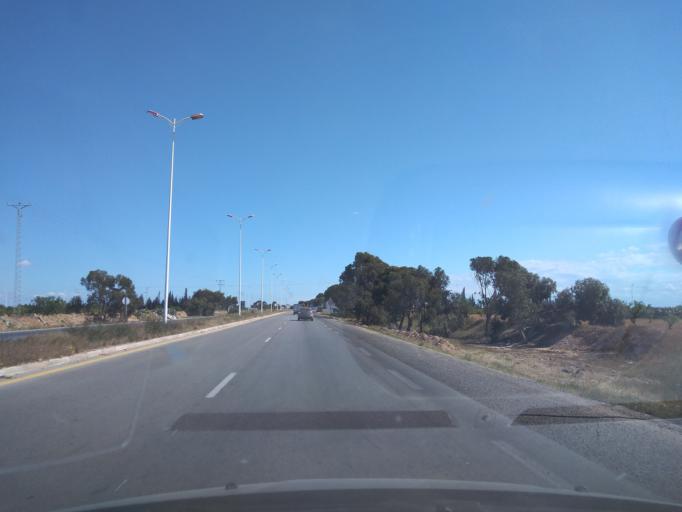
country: TN
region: Safaqis
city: Sfax
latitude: 34.8298
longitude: 10.7233
